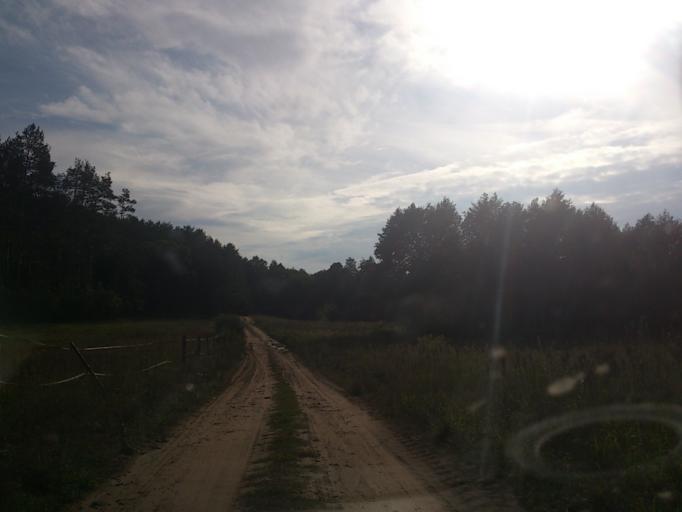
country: PL
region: Kujawsko-Pomorskie
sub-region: Powiat golubsko-dobrzynski
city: Golub-Dobrzyn
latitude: 53.1270
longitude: 19.1224
